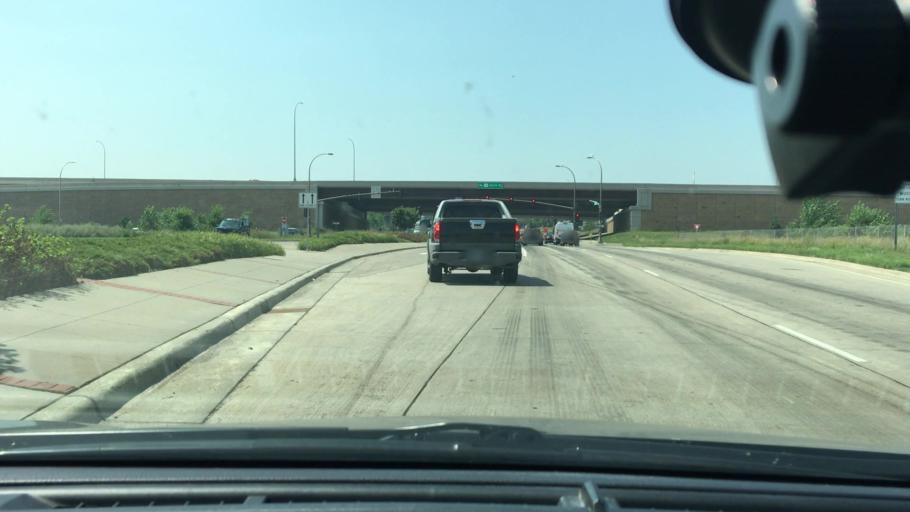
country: US
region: Minnesota
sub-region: Hennepin County
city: Osseo
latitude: 45.1090
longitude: -93.3893
